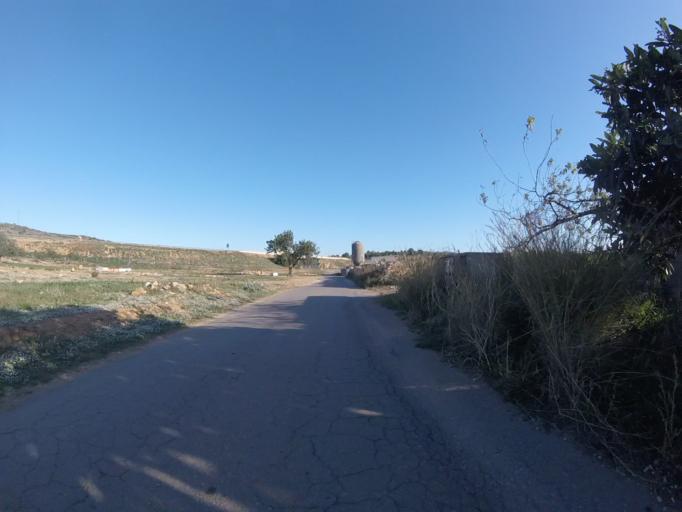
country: ES
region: Valencia
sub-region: Provincia de Castello
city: Torreblanca
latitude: 40.2299
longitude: 0.2013
